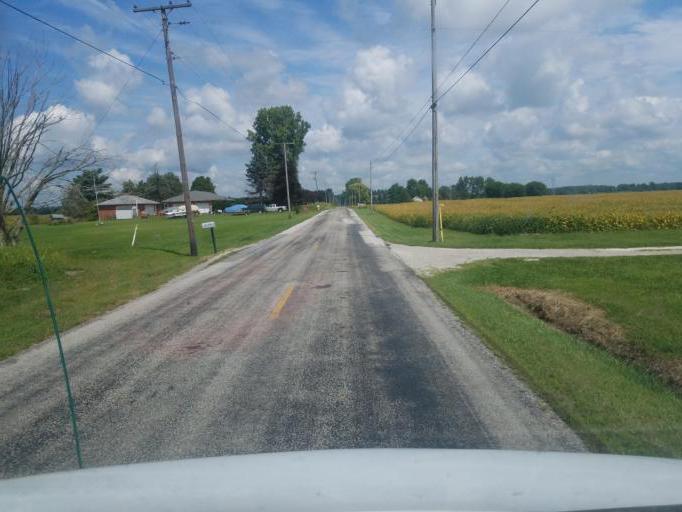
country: US
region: Ohio
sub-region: Marion County
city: Prospect
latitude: 40.5054
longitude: -83.1313
